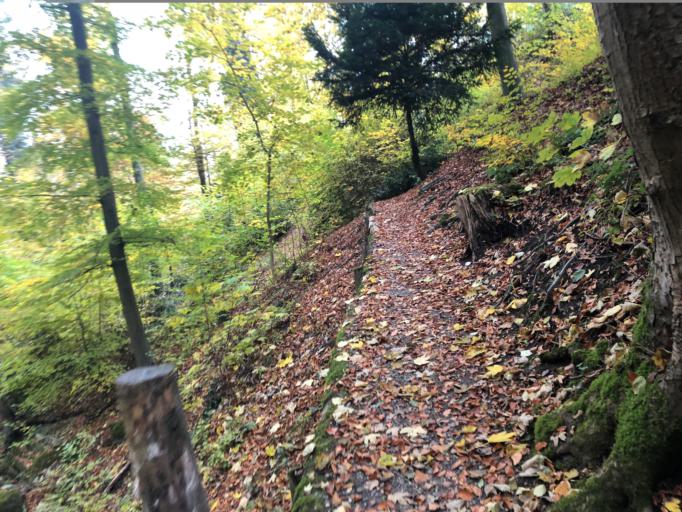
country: CH
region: Zurich
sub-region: Bezirk Meilen
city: Zollikon
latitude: 47.3336
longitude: 8.5766
